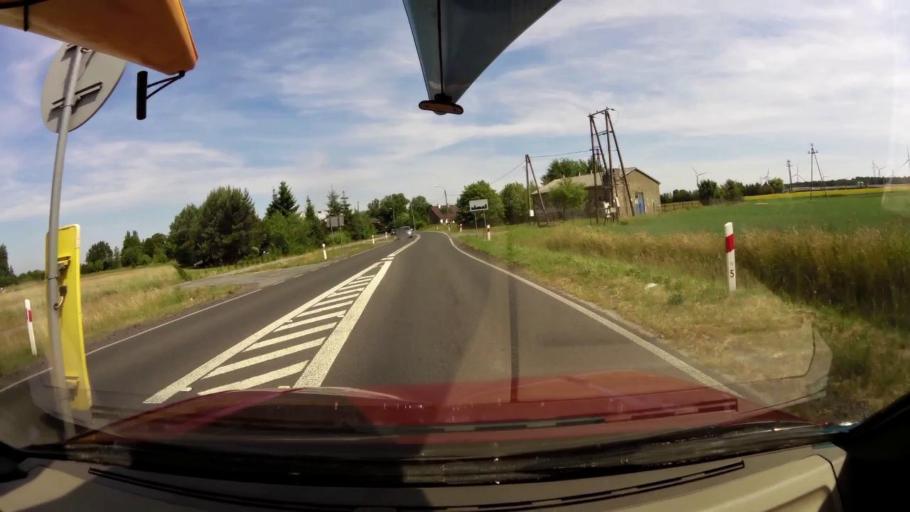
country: PL
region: West Pomeranian Voivodeship
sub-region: Powiat koszalinski
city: Sianow
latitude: 54.3079
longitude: 16.3072
